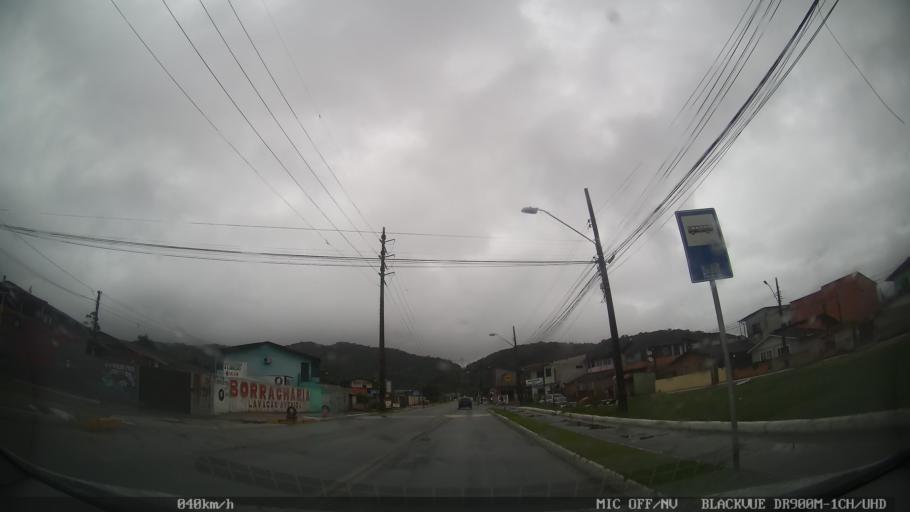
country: BR
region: Santa Catarina
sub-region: Itajai
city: Itajai
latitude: -26.9291
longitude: -48.6927
